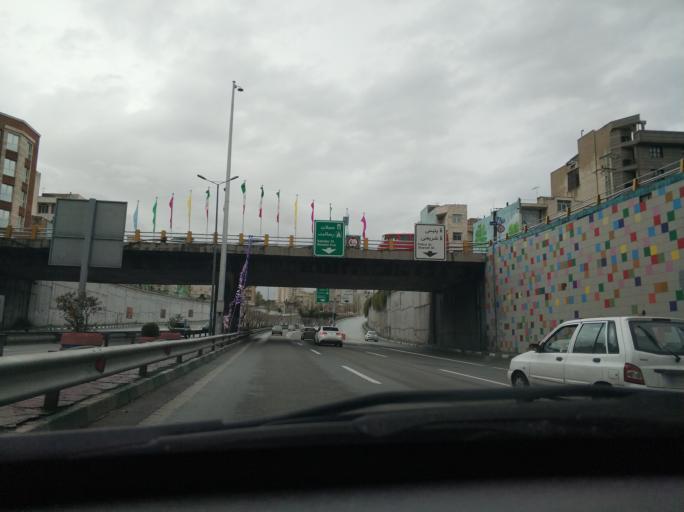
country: IR
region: Tehran
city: Tehran
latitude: 35.7189
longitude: 51.4477
